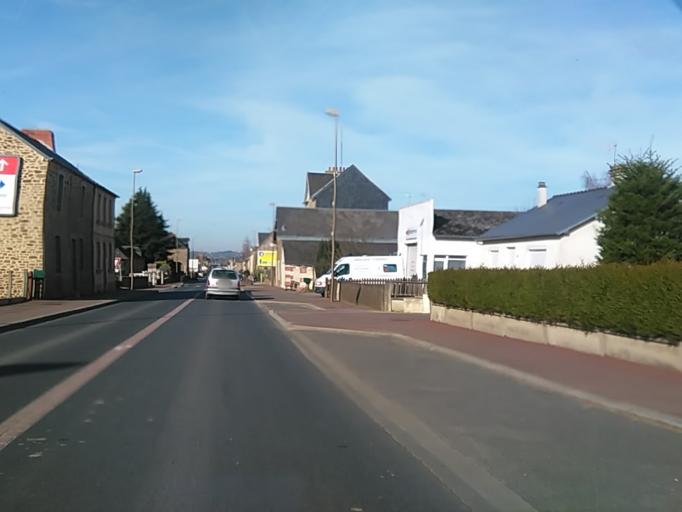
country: FR
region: Lower Normandy
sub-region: Departement de la Manche
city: Ducey
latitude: 48.6171
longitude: -1.2837
